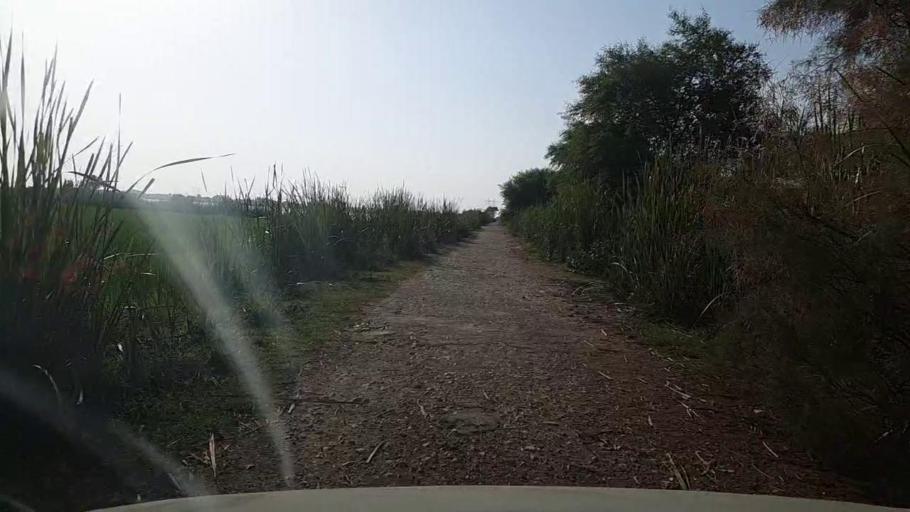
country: PK
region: Sindh
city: Kandhkot
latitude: 28.2889
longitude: 69.3290
